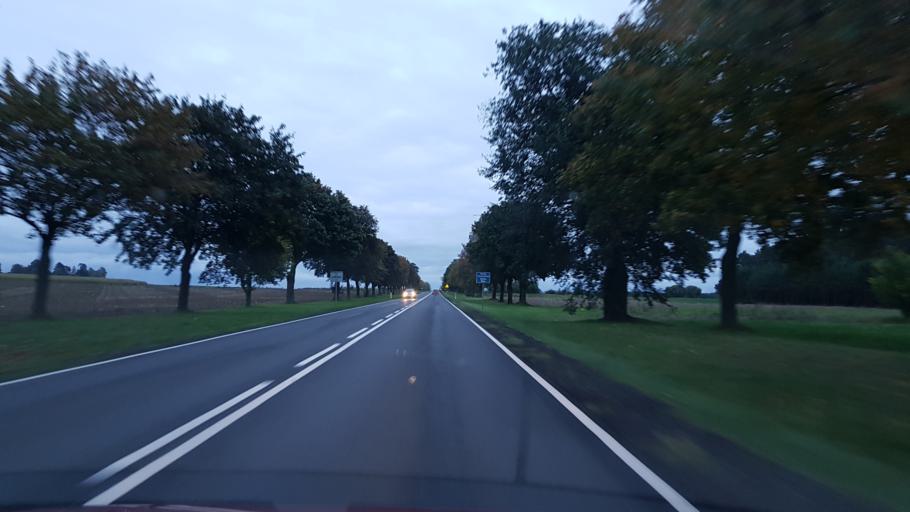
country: PL
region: West Pomeranian Voivodeship
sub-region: Powiat choszczenski
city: Recz
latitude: 53.2707
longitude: 15.4901
